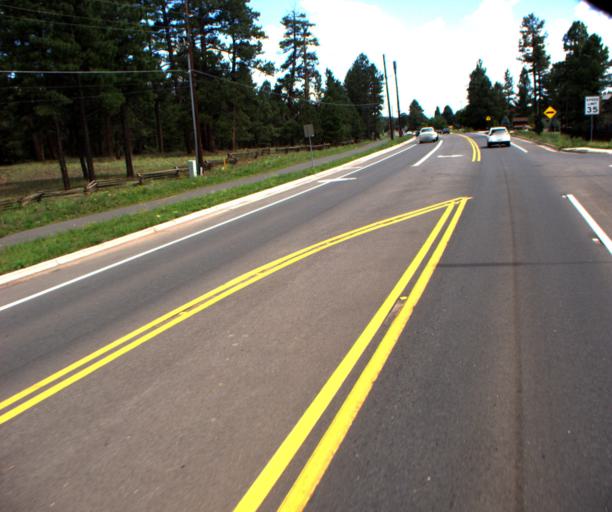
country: US
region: Arizona
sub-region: Coconino County
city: Flagstaff
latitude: 35.2284
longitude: -111.6599
